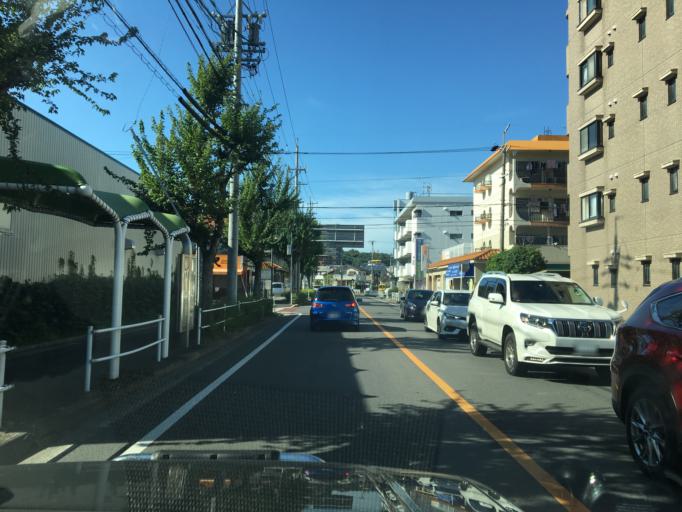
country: JP
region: Aichi
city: Kasugai
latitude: 35.2026
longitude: 136.9980
